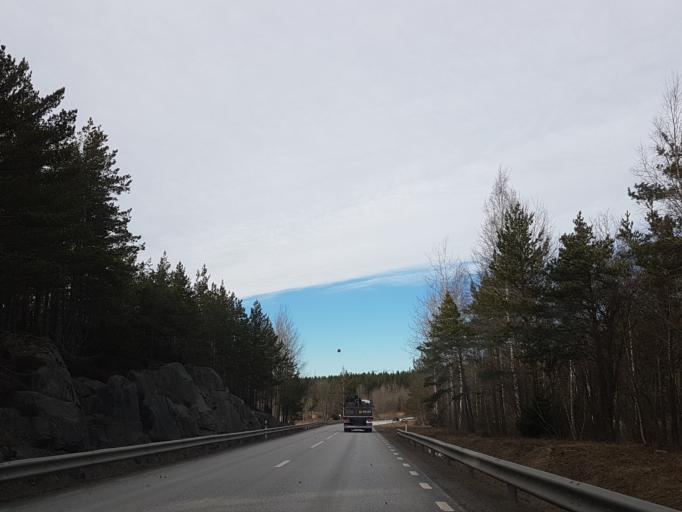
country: SE
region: Stockholm
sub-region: Norrtalje Kommun
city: Norrtalje
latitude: 59.7182
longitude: 18.6702
